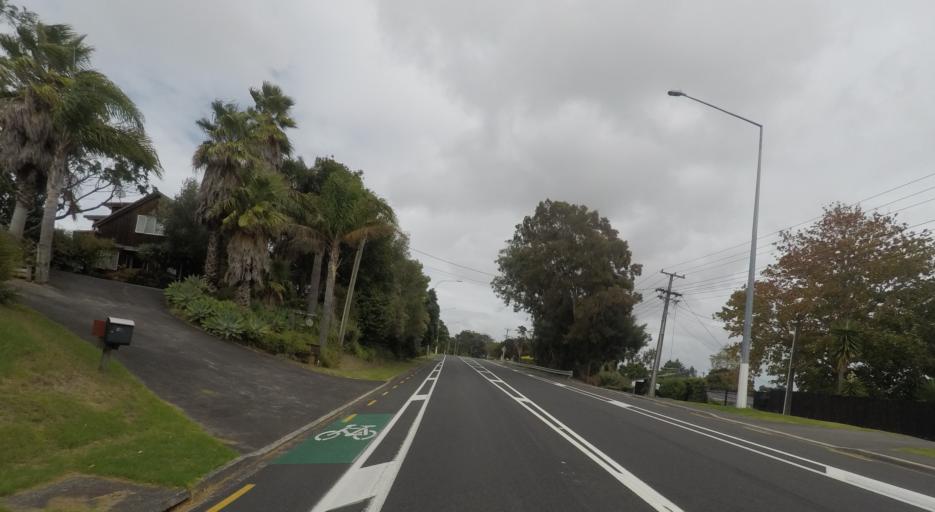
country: NZ
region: Auckland
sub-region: Auckland
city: North Shore
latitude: -36.7721
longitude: 174.6936
